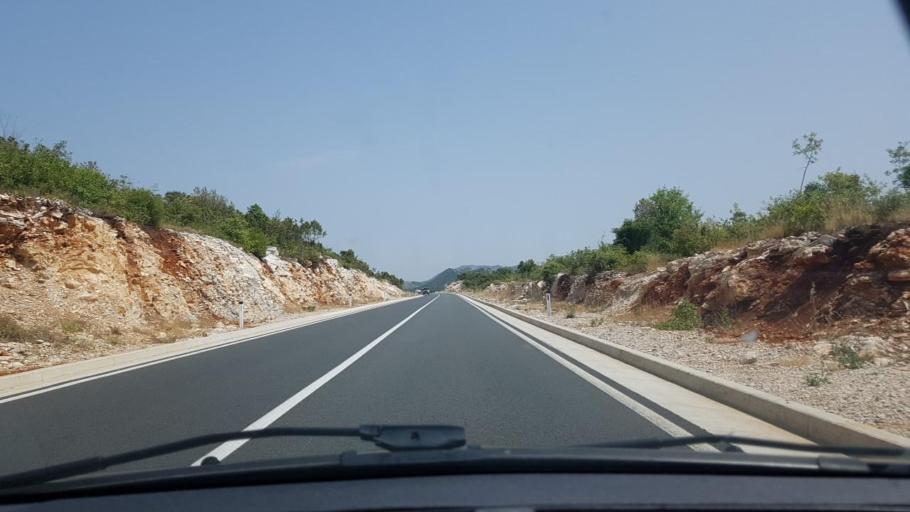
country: BA
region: Federation of Bosnia and Herzegovina
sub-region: Hercegovacko-Bosanski Kanton
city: Neum
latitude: 42.9577
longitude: 17.7238
